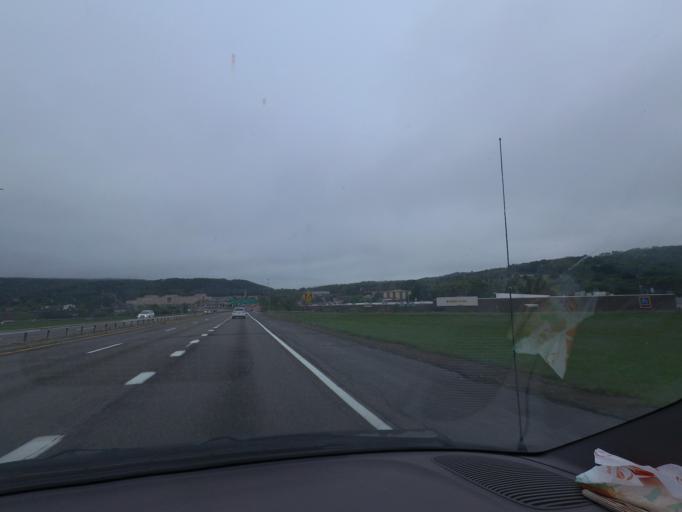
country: US
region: New York
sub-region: Broome County
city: Johnson City
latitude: 42.1213
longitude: -75.9700
